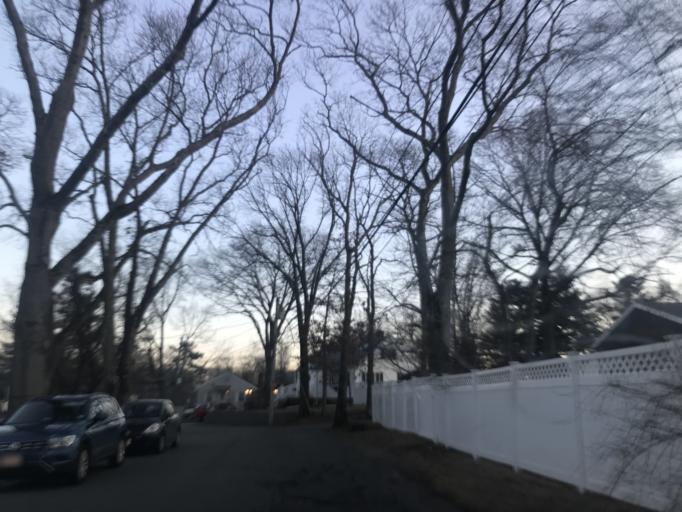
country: US
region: Massachusetts
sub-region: Essex County
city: Saugus
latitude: 42.4760
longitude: -71.0047
